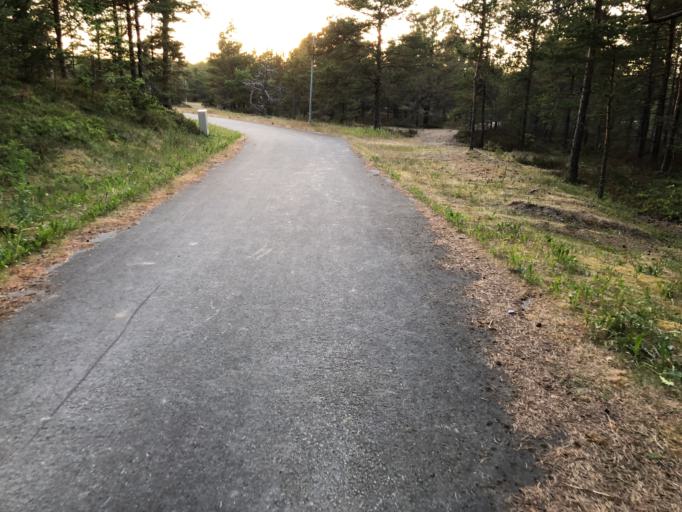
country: EE
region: Harju
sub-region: Paldiski linn
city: Paldiski
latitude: 59.3918
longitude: 24.2328
